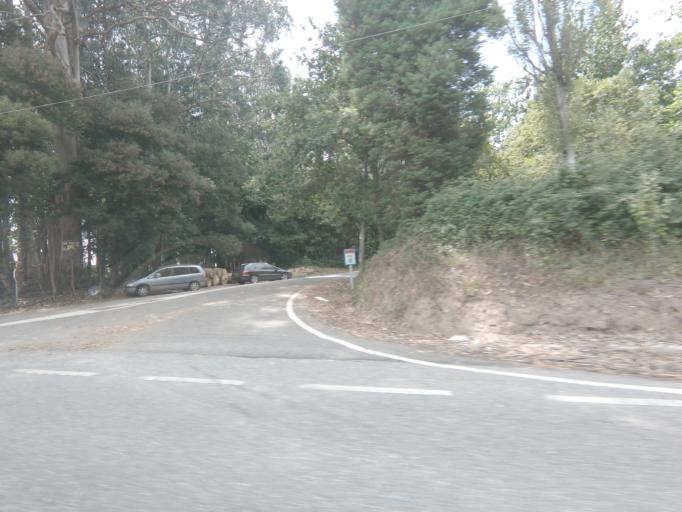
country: PT
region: Viana do Castelo
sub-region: Valenca
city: Valenca
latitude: 42.0274
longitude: -8.6760
